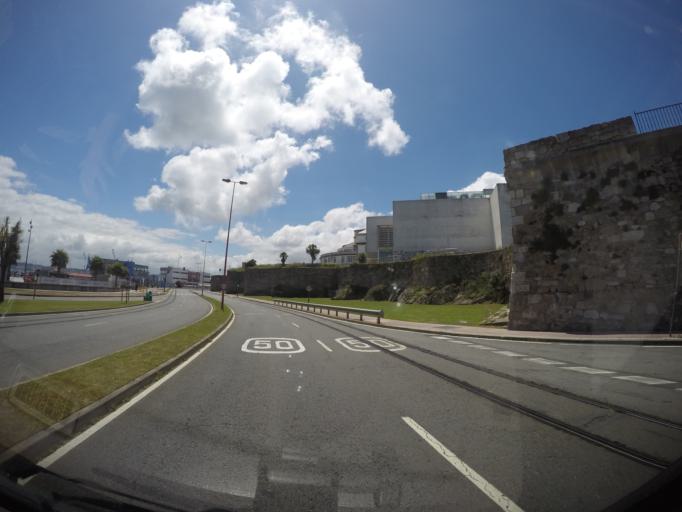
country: ES
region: Galicia
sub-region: Provincia da Coruna
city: A Coruna
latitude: 43.3677
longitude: -8.3891
